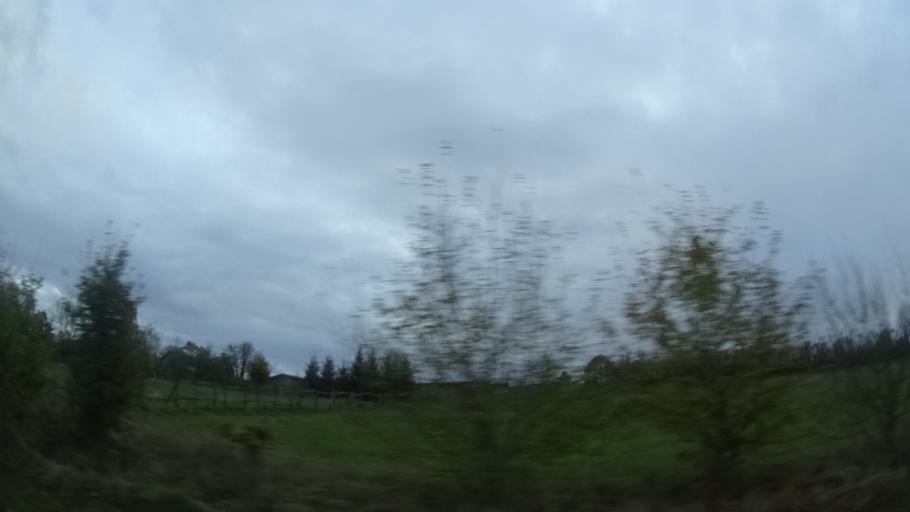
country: DE
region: Hesse
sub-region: Regierungsbezirk Giessen
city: Freiensteinau
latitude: 50.4014
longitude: 9.4226
